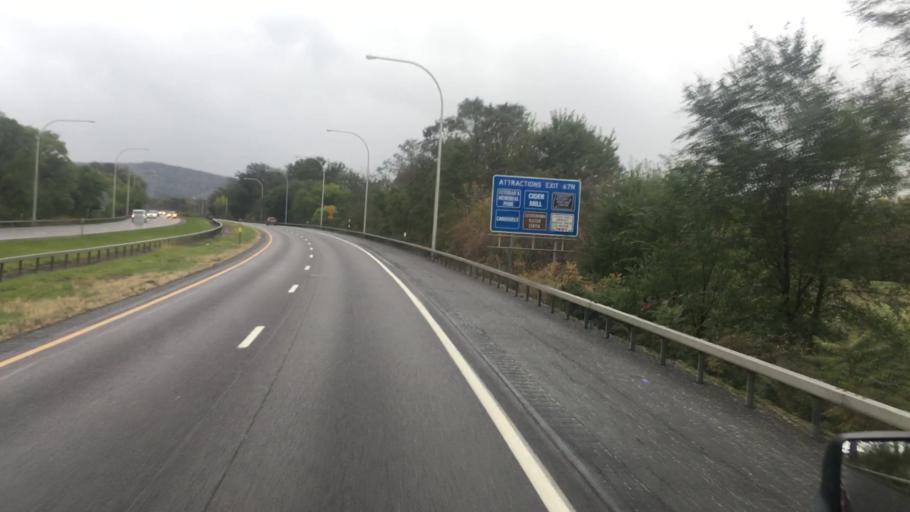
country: US
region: New York
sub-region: Broome County
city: Endwell
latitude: 42.0993
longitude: -76.0276
